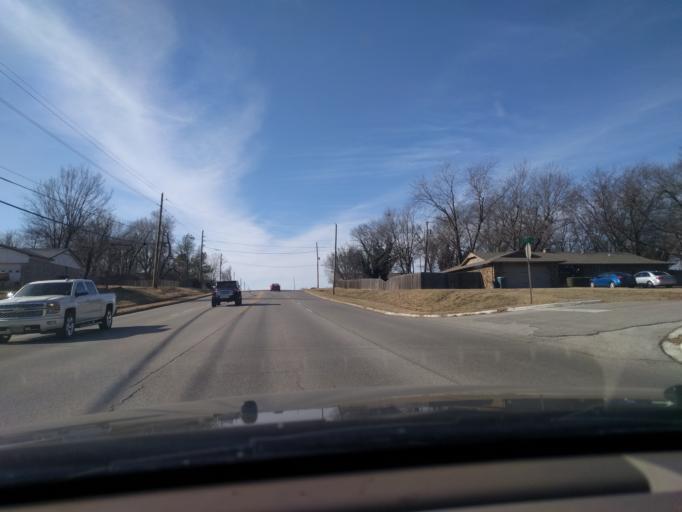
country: US
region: Oklahoma
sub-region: Tulsa County
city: Broken Arrow
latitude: 36.0609
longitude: -95.7202
